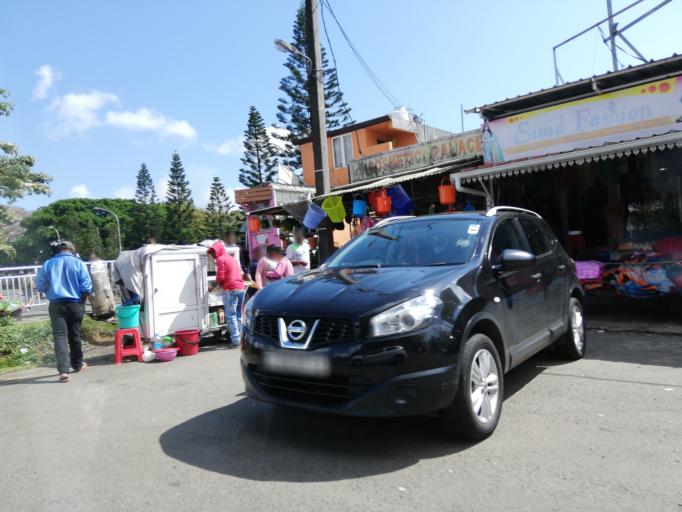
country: MU
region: Moka
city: Verdun
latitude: -20.2247
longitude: 57.5403
